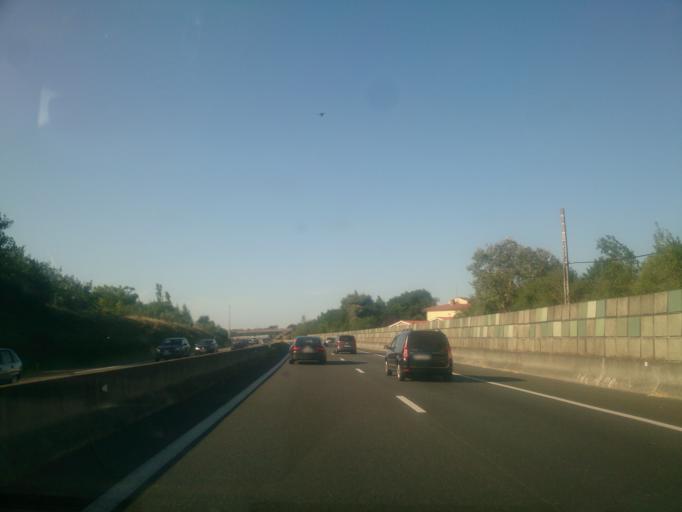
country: FR
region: Midi-Pyrenees
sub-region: Departement du Tarn-et-Garonne
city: Montauban
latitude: 44.0139
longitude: 1.3872
